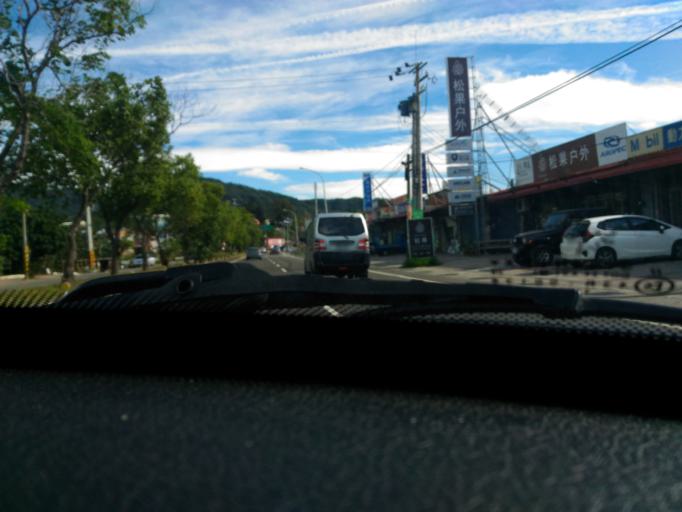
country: TW
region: Taiwan
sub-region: Hsinchu
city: Zhubei
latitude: 24.7639
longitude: 121.0869
